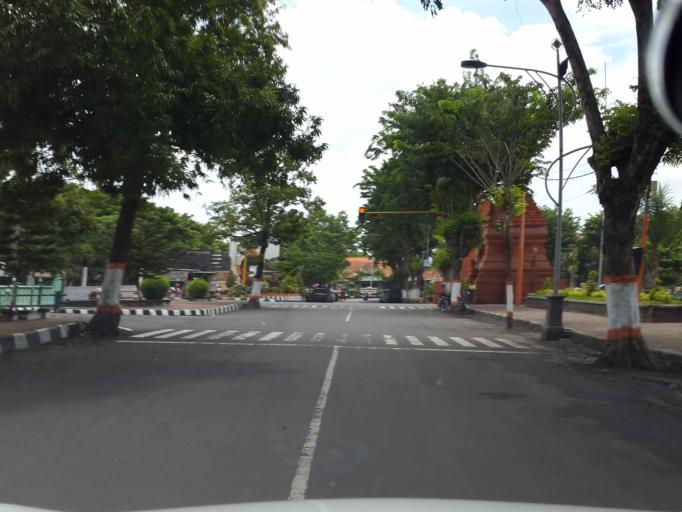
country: ID
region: East Java
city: Mojokerto
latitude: -7.4627
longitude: 112.4313
